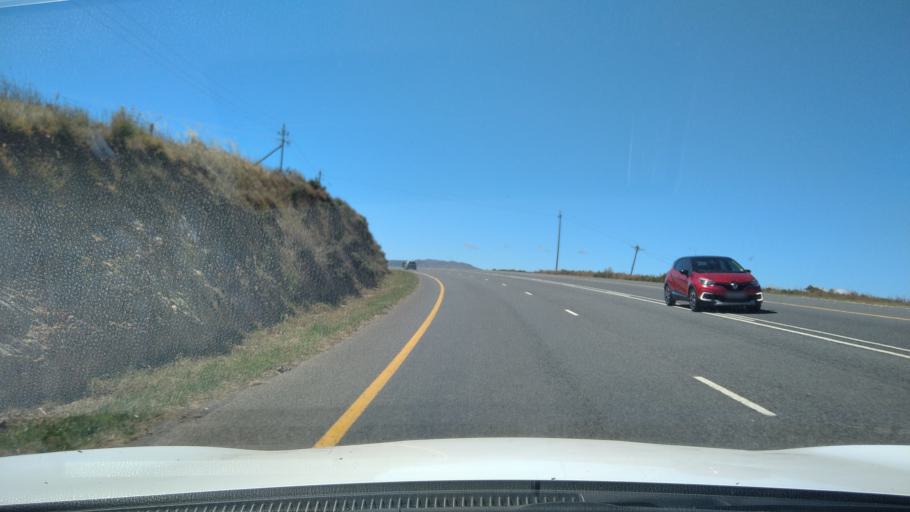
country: ZA
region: Western Cape
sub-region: Overberg District Municipality
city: Caledon
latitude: -34.2151
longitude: 19.4004
